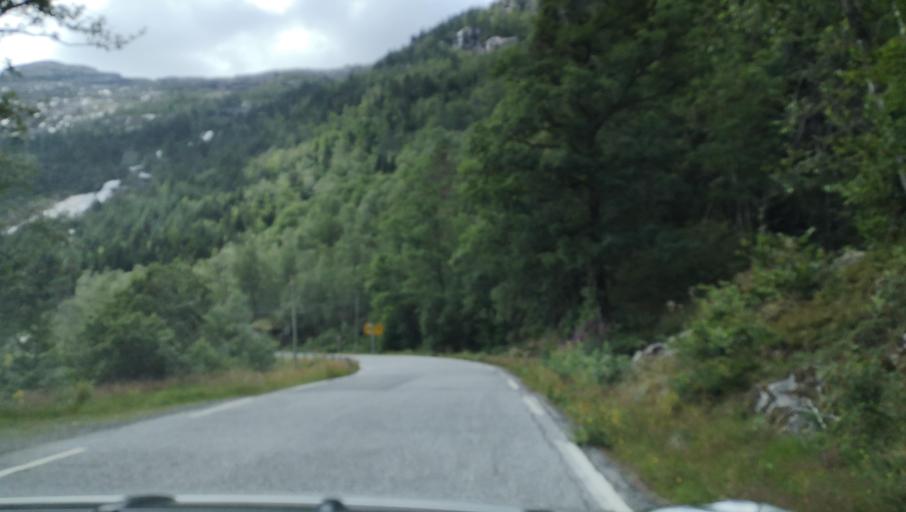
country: NO
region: Hordaland
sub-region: Modalen
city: Mo
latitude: 60.7854
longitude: 5.8413
